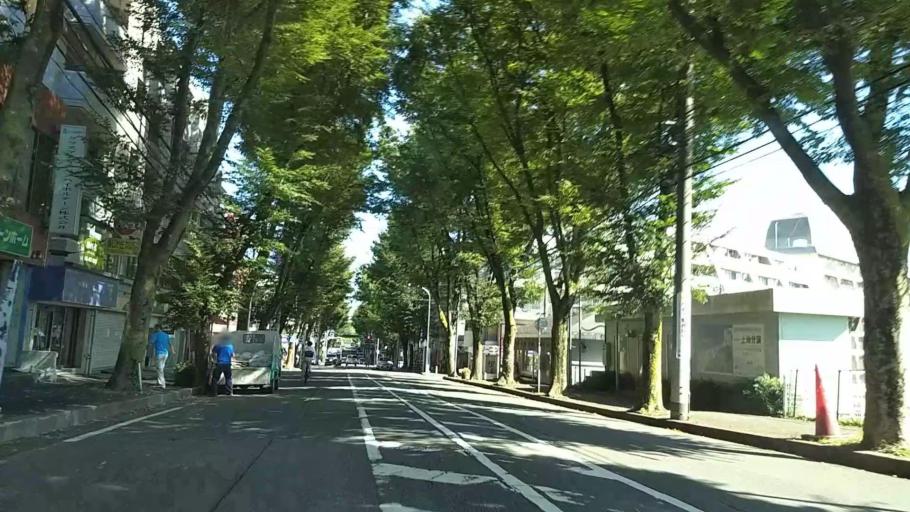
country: JP
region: Tokyo
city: Chofugaoka
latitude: 35.5762
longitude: 139.5557
